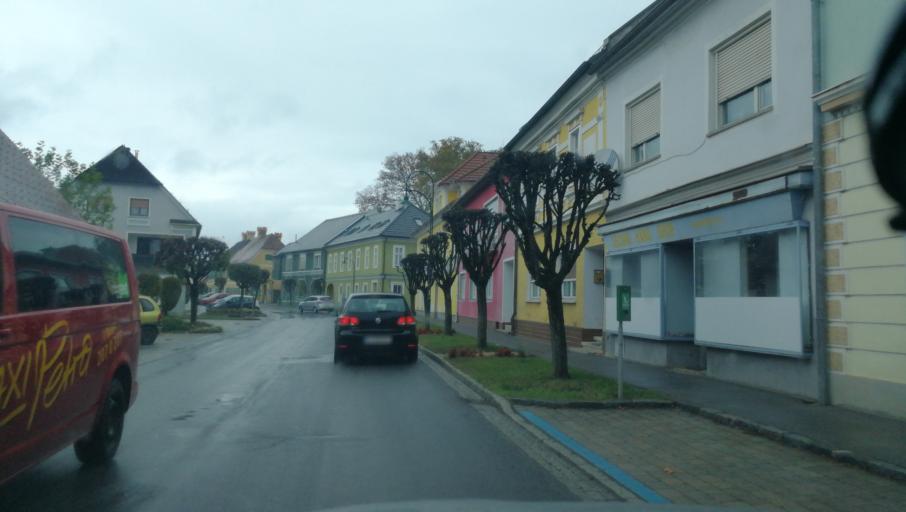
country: AT
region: Styria
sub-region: Politischer Bezirk Leibnitz
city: Strass in Steiermark
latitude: 46.7281
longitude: 15.6213
